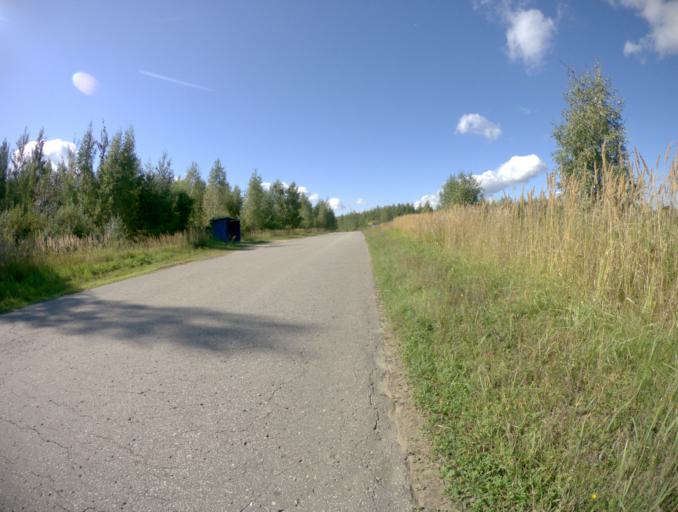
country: RU
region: Vladimir
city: Lakinsk
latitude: 55.8908
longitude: 39.8630
